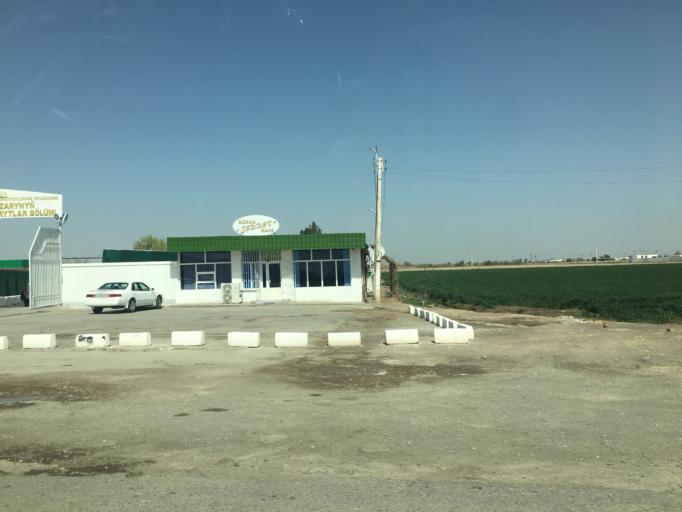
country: TM
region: Lebap
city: Turkmenabat
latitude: 39.0134
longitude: 63.6015
